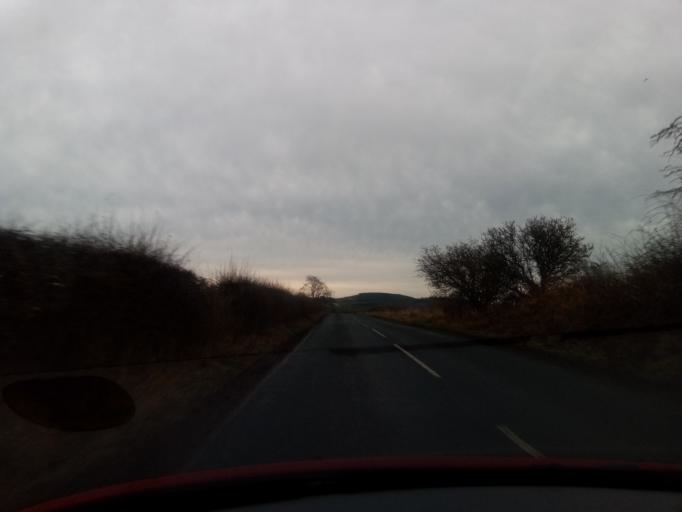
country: GB
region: England
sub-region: Northumberland
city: Ellingham
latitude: 55.4604
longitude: -1.7886
